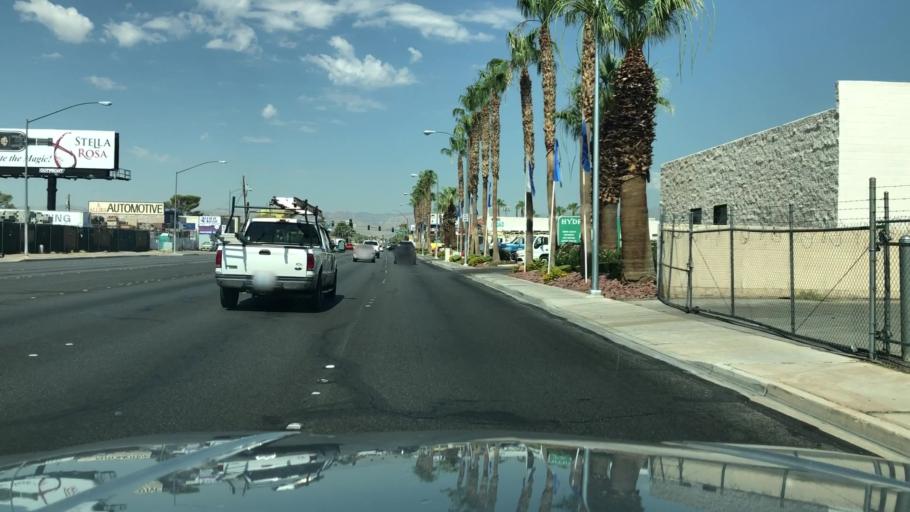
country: US
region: Nevada
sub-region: Clark County
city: Paradise
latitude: 36.1303
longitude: -115.1923
